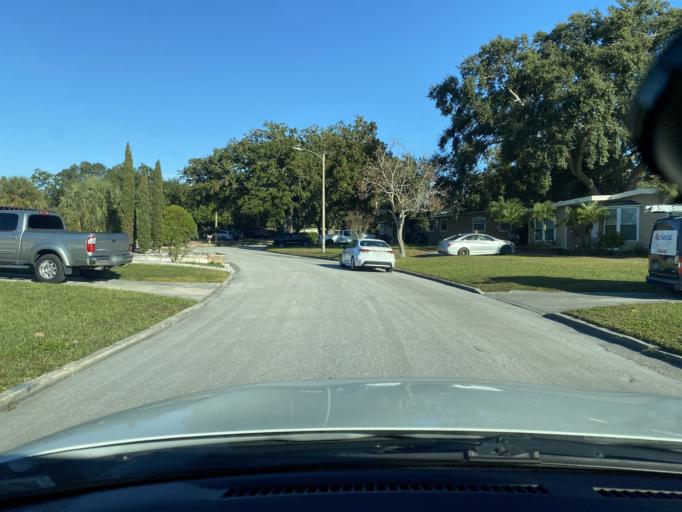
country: US
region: Florida
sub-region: Orange County
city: Azalea Park
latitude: 28.5332
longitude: -81.3027
